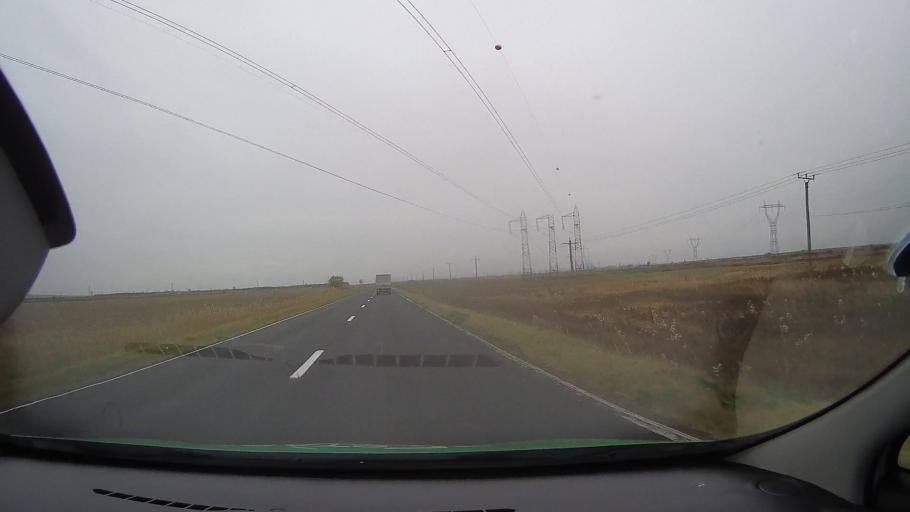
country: RO
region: Ialomita
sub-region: Comuna Gura Ialomitei
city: Gura Ialomitei
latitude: 44.6893
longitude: 27.7998
